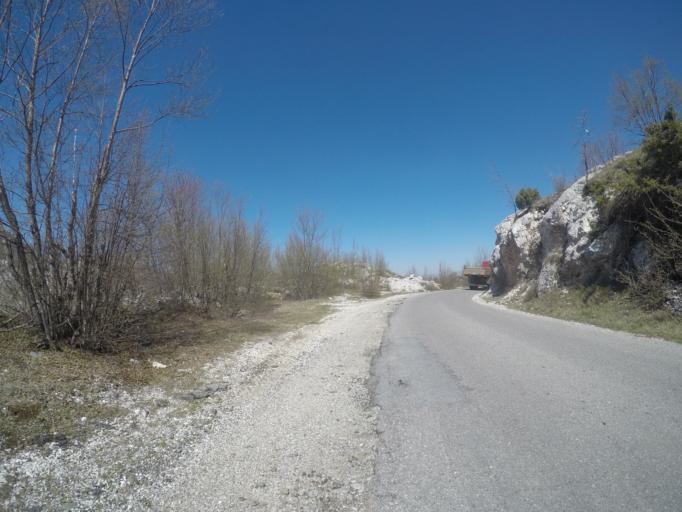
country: ME
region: Cetinje
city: Cetinje
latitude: 42.4441
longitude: 18.8736
